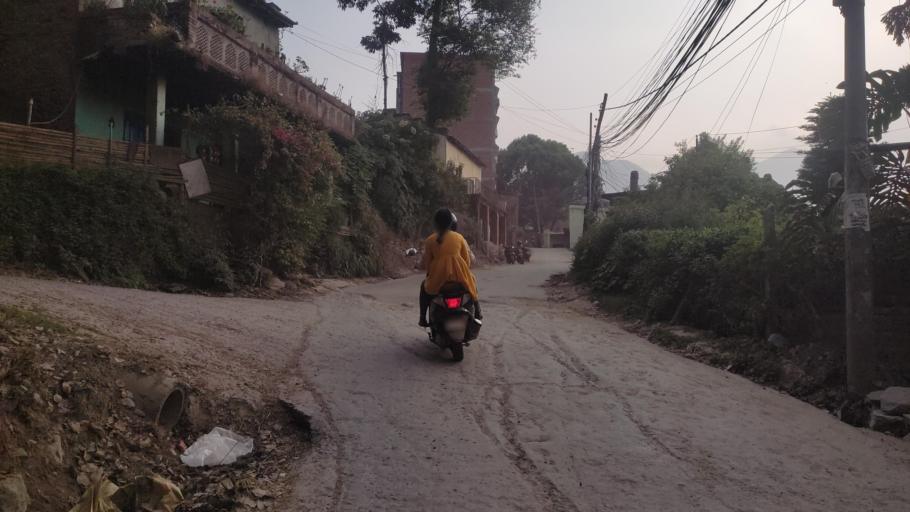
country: NP
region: Central Region
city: Kirtipur
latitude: 27.6699
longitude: 85.2879
